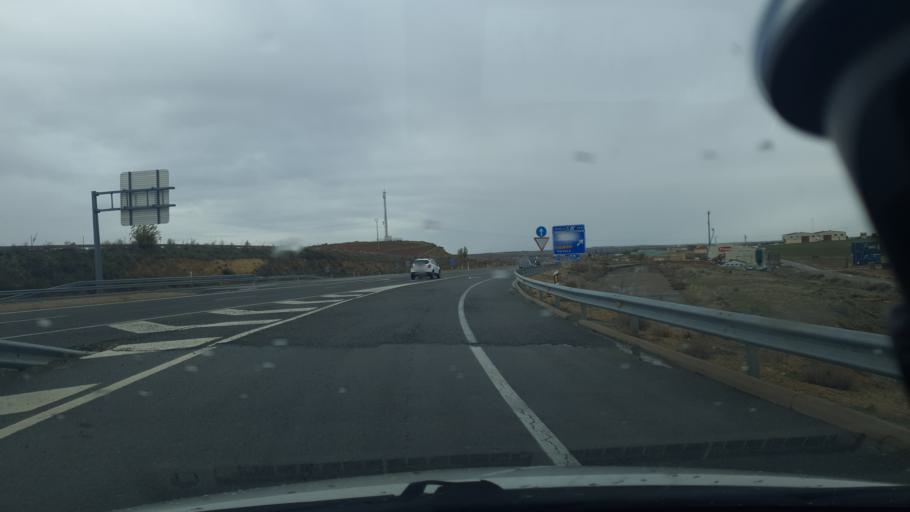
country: ES
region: Castille and Leon
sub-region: Provincia de Segovia
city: Encinillas
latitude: 40.9928
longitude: -4.1425
